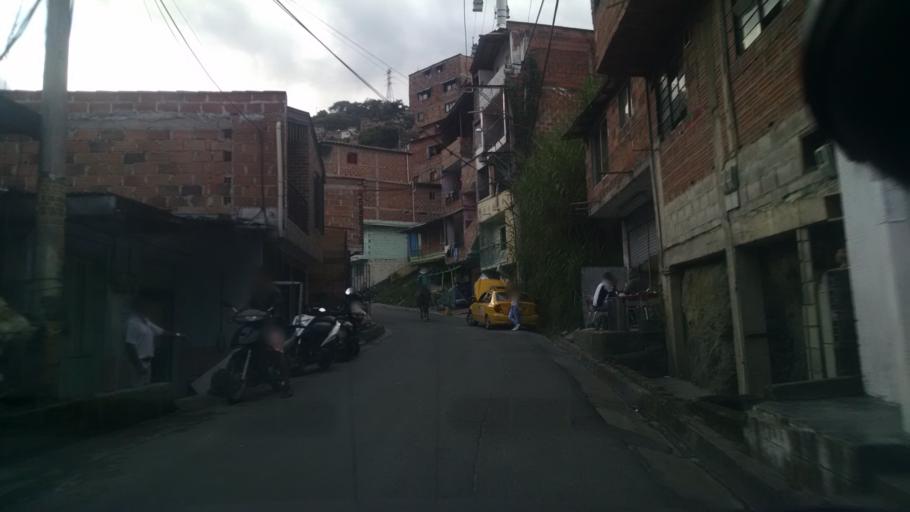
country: CO
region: Antioquia
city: Medellin
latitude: 6.2668
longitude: -75.6138
